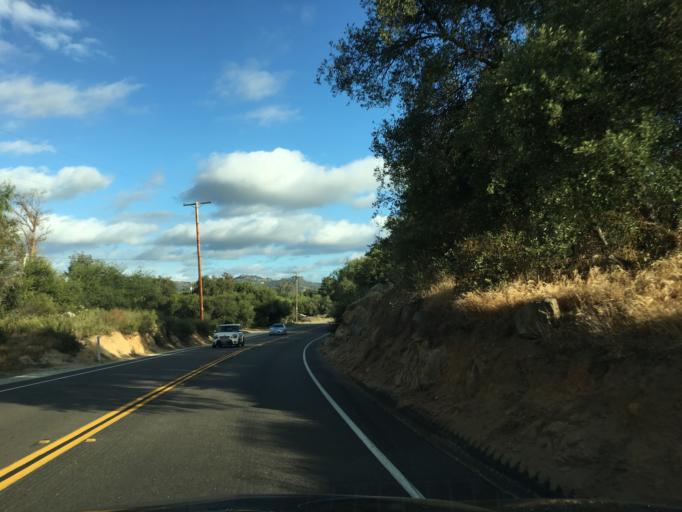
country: US
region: California
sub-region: San Diego County
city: Valley Center
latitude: 33.2290
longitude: -117.0428
